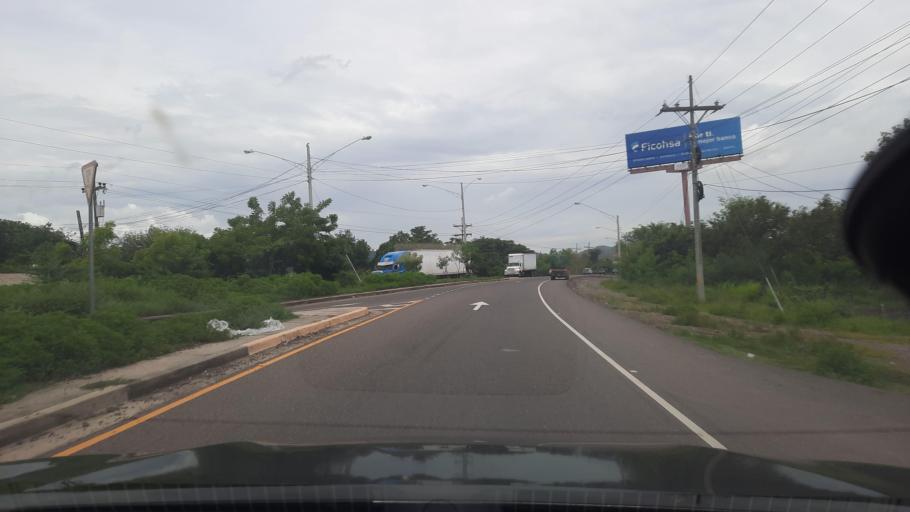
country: HN
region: Valle
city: Jicaro Galan
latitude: 13.5292
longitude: -87.4390
